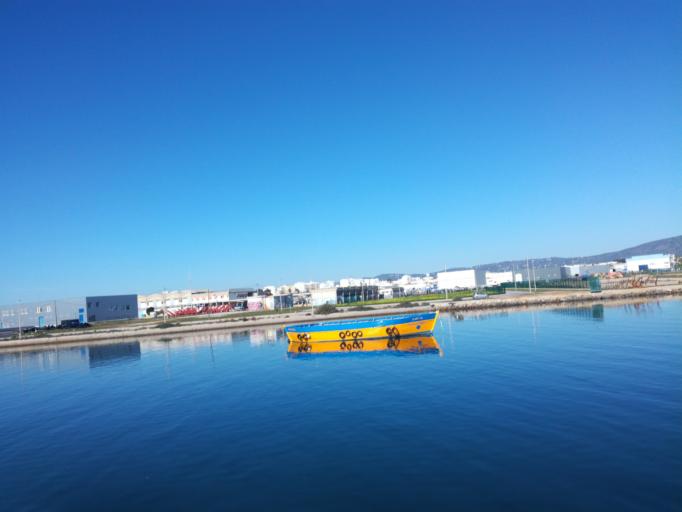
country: PT
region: Faro
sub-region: Olhao
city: Olhao
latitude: 37.0242
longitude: -7.8306
